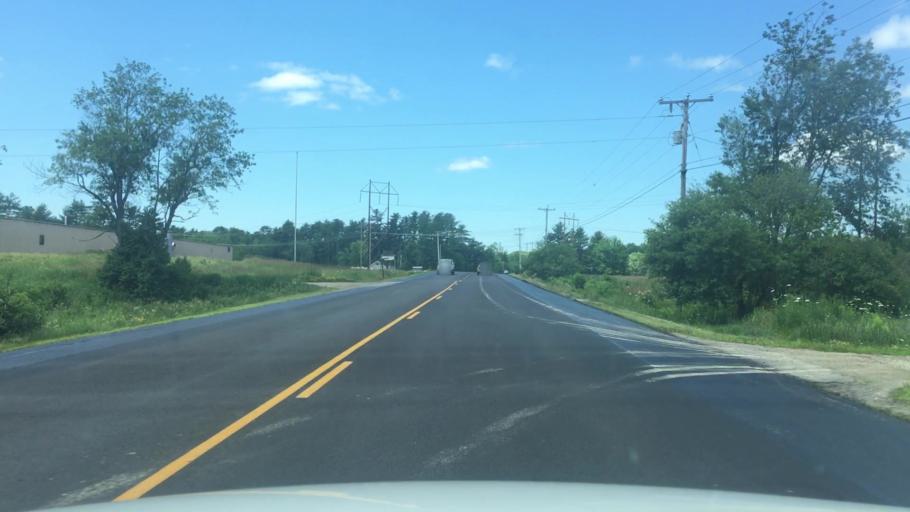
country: US
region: Maine
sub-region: Waldo County
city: Searsmont
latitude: 44.4060
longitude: -69.2019
